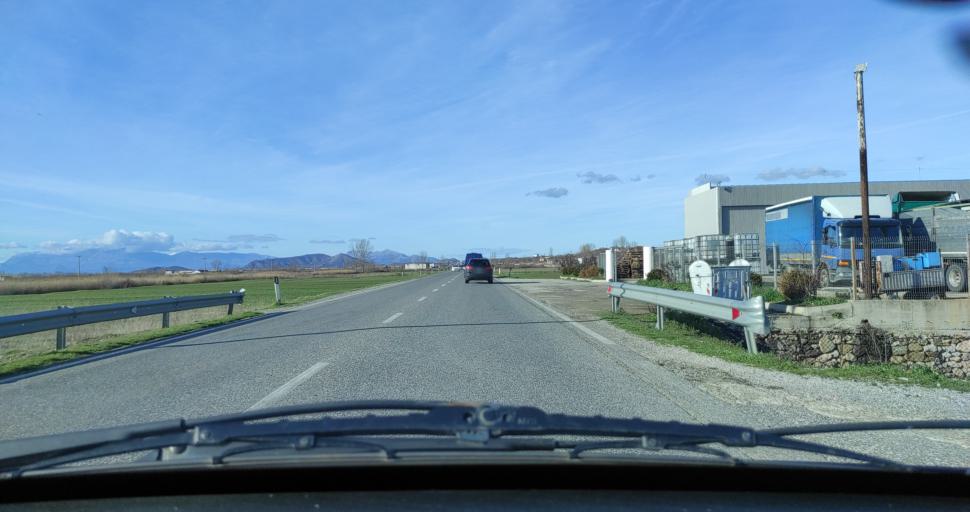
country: AL
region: Lezhe
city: Shengjin
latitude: 41.8574
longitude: 19.5666
